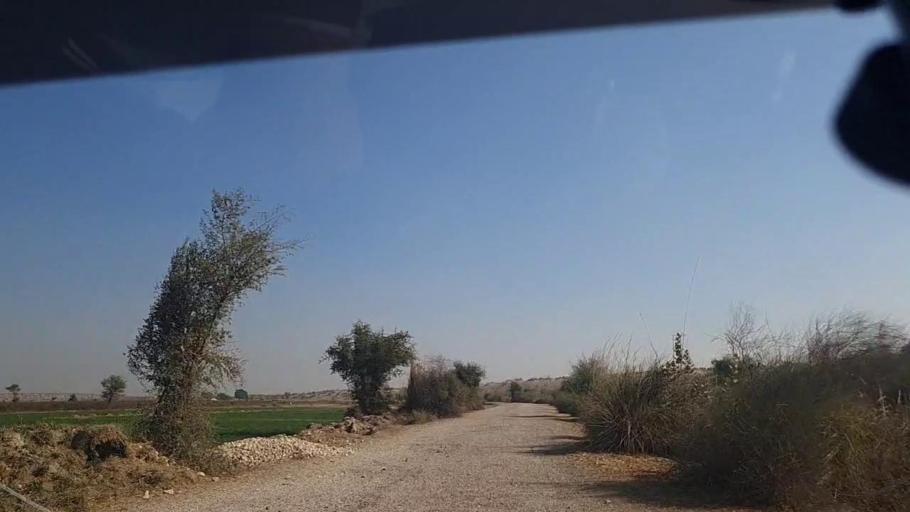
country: PK
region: Sindh
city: Khanpur
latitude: 27.5593
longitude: 69.3266
